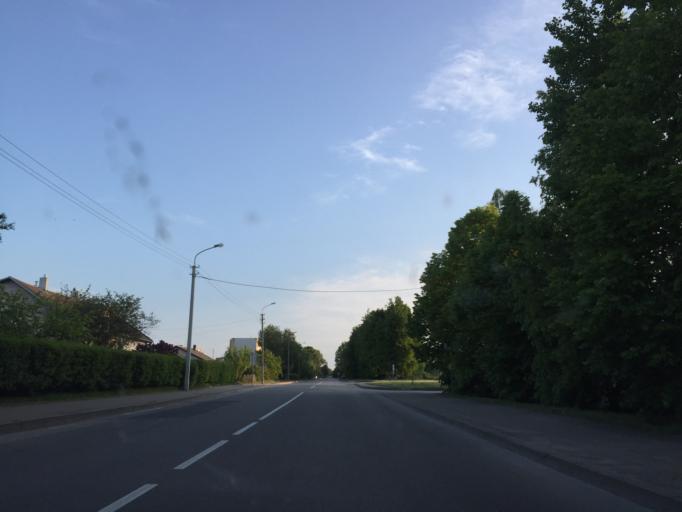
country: LT
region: Siauliu apskritis
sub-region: Siauliai
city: Siauliai
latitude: 55.9534
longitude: 23.3282
